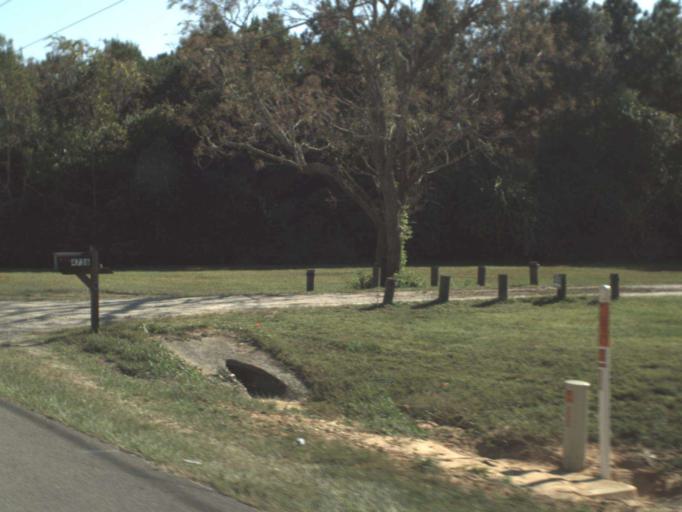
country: US
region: Florida
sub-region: Walton County
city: DeFuniak Springs
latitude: 30.6550
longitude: -86.1167
